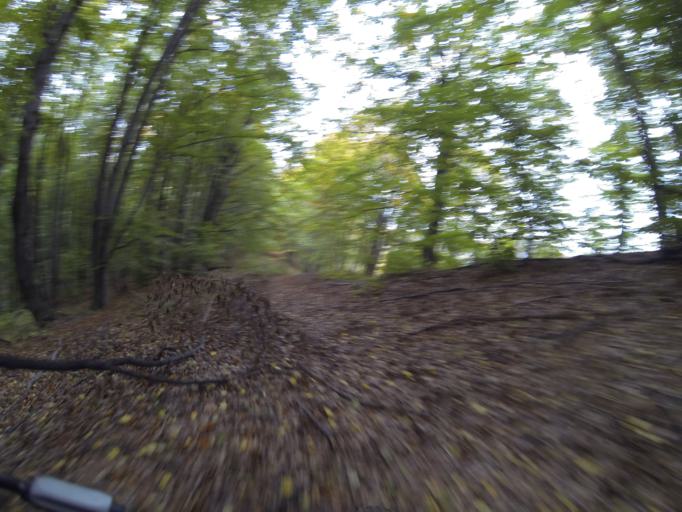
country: RO
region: Gorj
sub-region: Comuna Tismana
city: Sohodol
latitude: 45.0915
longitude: 22.8860
